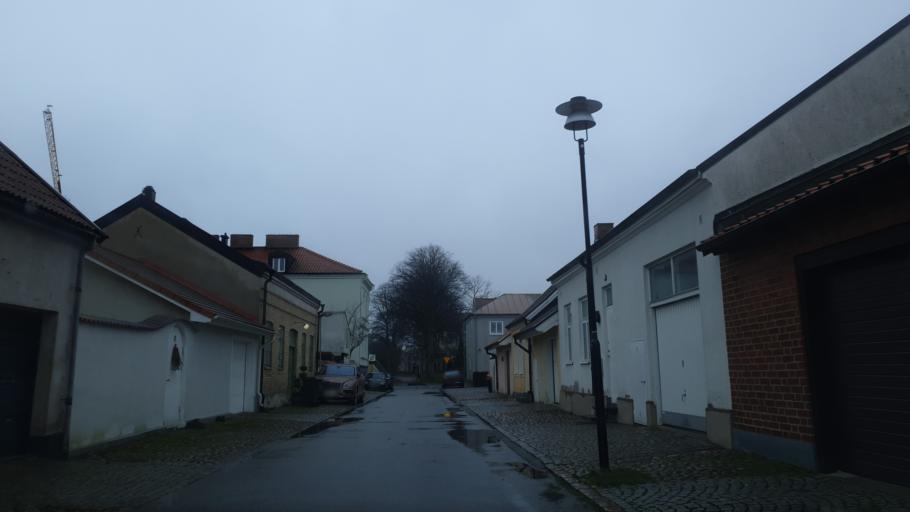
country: SE
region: Skane
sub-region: Ystads Kommun
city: Ystad
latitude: 55.4293
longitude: 13.8307
